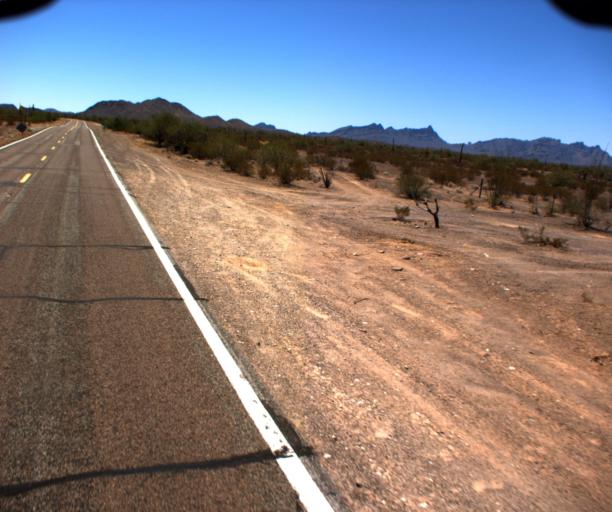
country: US
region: Arizona
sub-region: Pima County
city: Ajo
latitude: 32.2316
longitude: -112.7135
